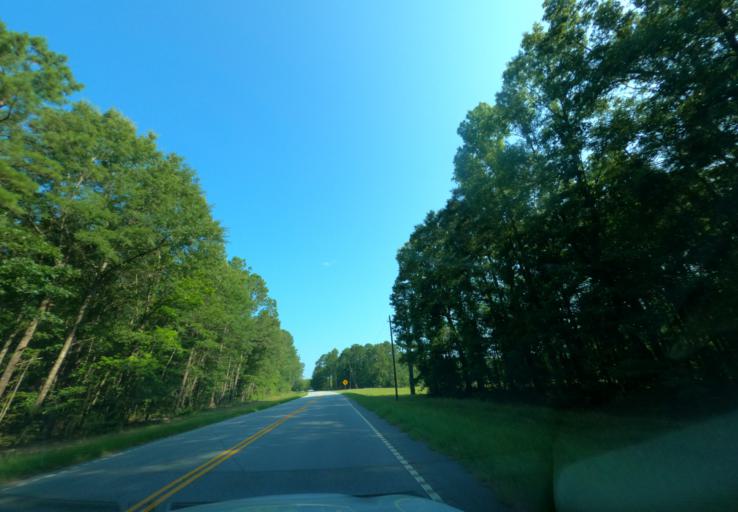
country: US
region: South Carolina
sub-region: Greenwood County
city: Ninety Six
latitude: 34.0326
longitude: -82.0422
